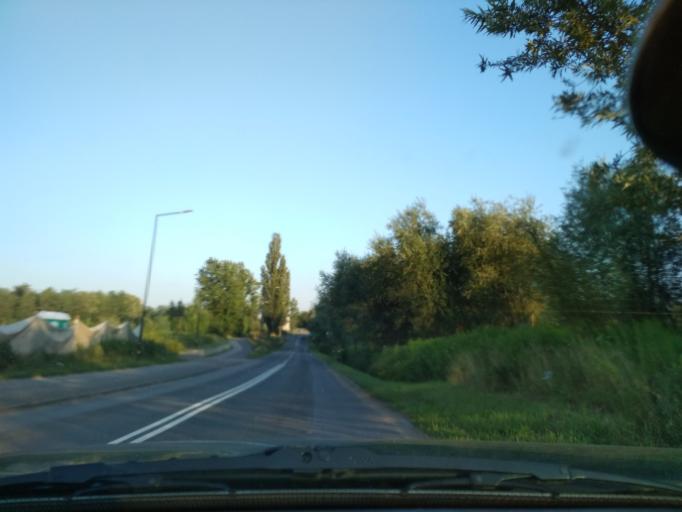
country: PL
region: Silesian Voivodeship
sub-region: Gliwice
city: Gliwice
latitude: 50.2739
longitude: 18.6832
